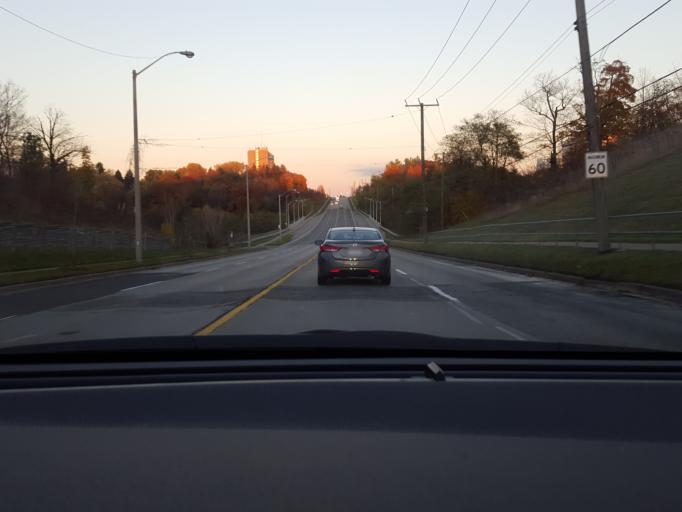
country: CA
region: Ontario
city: Scarborough
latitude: 43.7804
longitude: -79.2143
